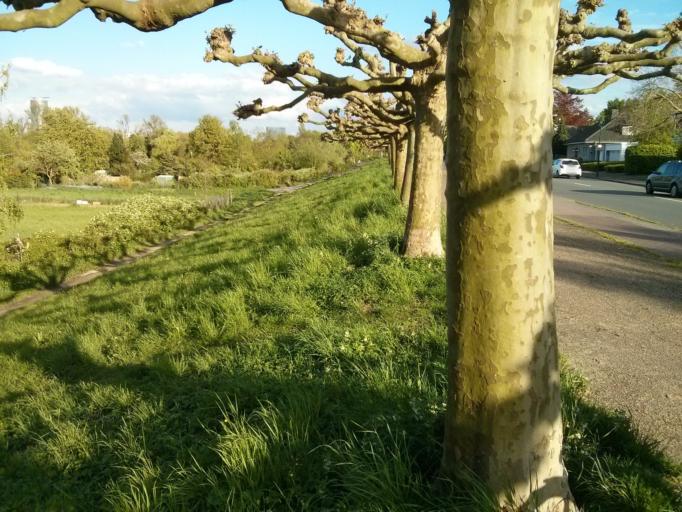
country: DE
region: North Rhine-Westphalia
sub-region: Regierungsbezirk Dusseldorf
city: Dusseldorf
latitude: 51.2405
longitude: 6.7552
